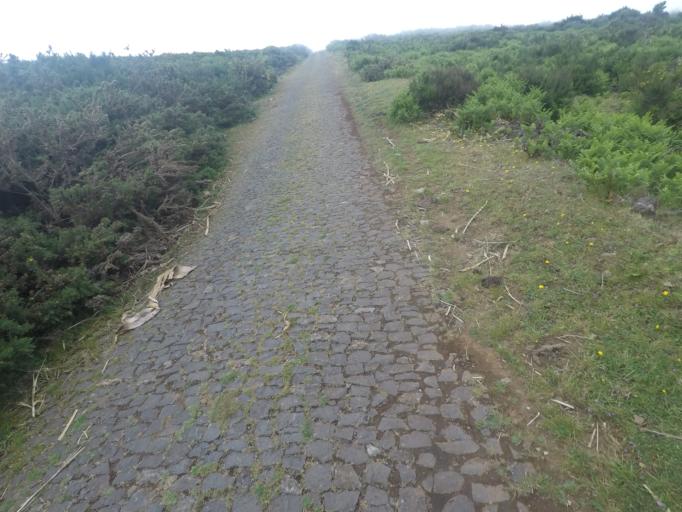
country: PT
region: Madeira
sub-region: Calheta
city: Arco da Calheta
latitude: 32.7367
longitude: -17.0990
